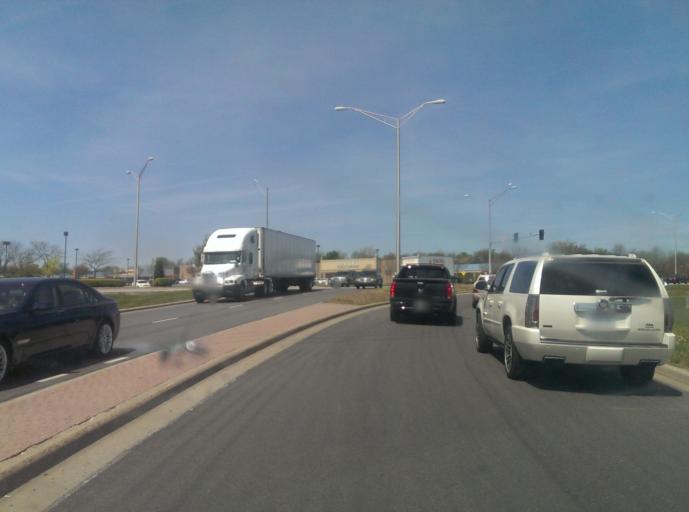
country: US
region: Kansas
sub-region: Johnson County
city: Overland Park
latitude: 38.9141
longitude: -94.6682
